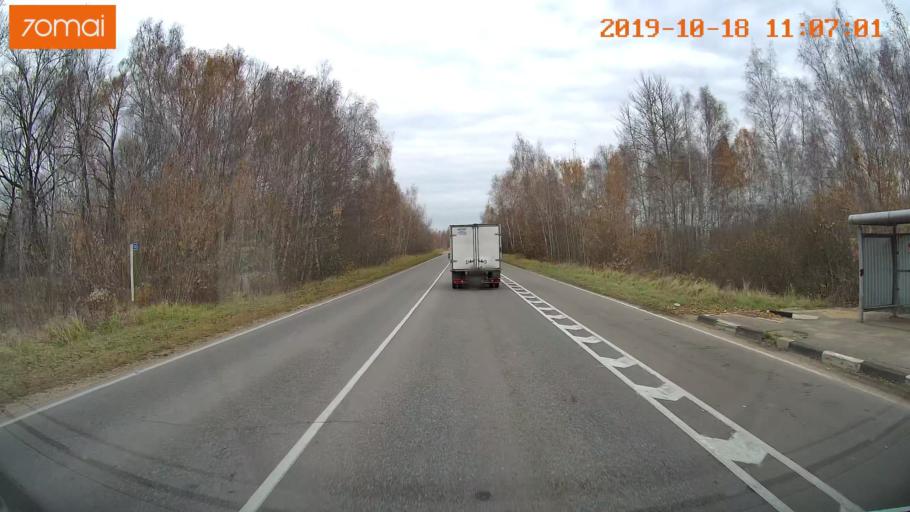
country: RU
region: Tula
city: Kimovsk
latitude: 53.9238
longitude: 38.5349
